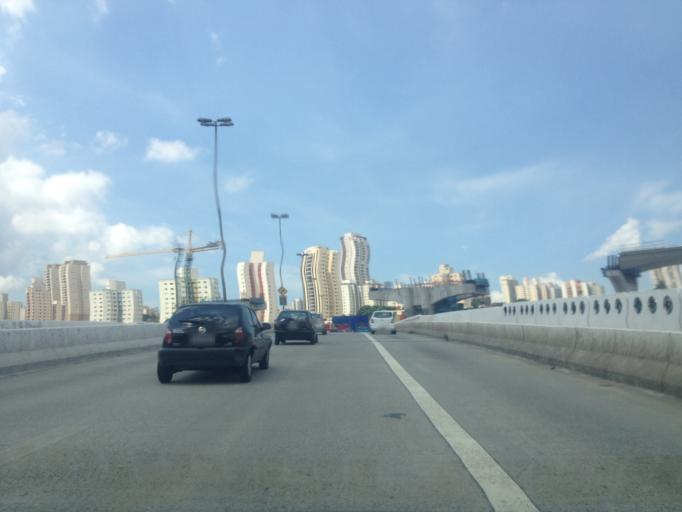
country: BR
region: Sao Paulo
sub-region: Diadema
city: Diadema
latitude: -23.6329
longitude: -46.6692
